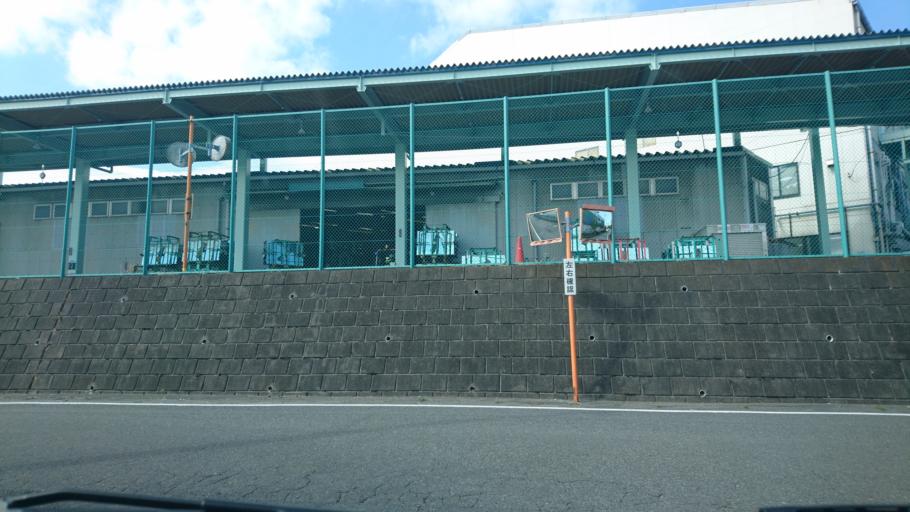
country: JP
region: Kanagawa
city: Zama
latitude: 35.5327
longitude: 139.3283
